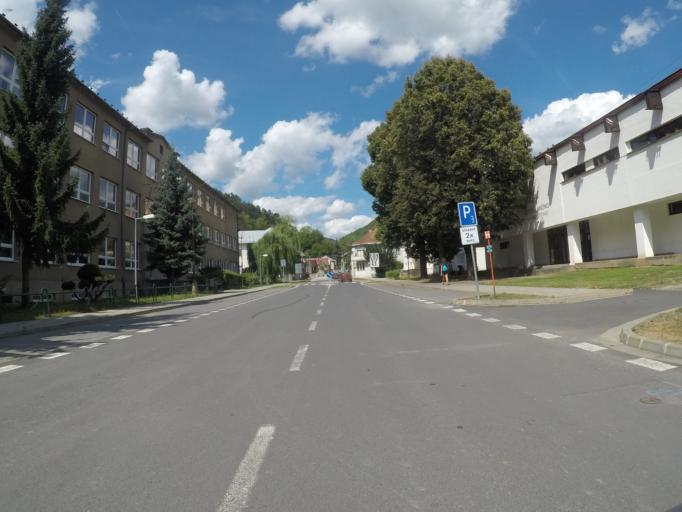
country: SK
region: Banskobystricky
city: Tisovec
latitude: 48.6796
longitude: 19.9405
